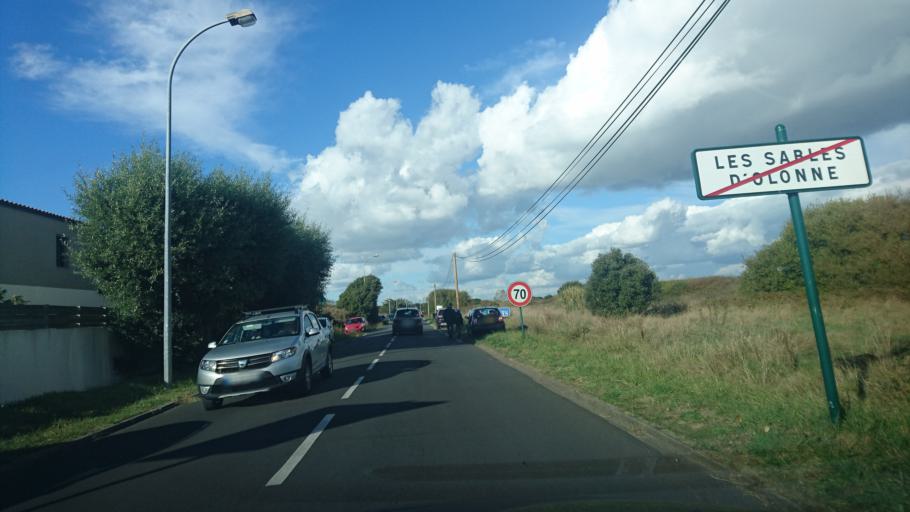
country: FR
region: Pays de la Loire
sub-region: Departement de la Vendee
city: Les Sables-d'Olonne
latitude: 46.5094
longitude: -1.8029
